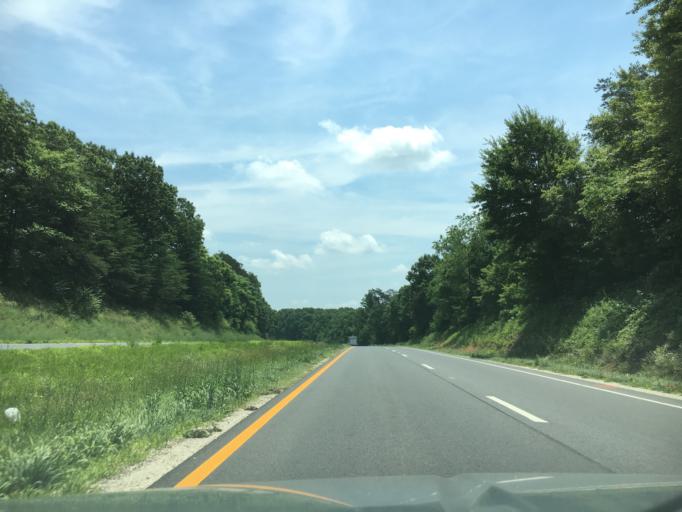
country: US
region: Virginia
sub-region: Campbell County
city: Concord
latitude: 37.3545
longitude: -78.9982
